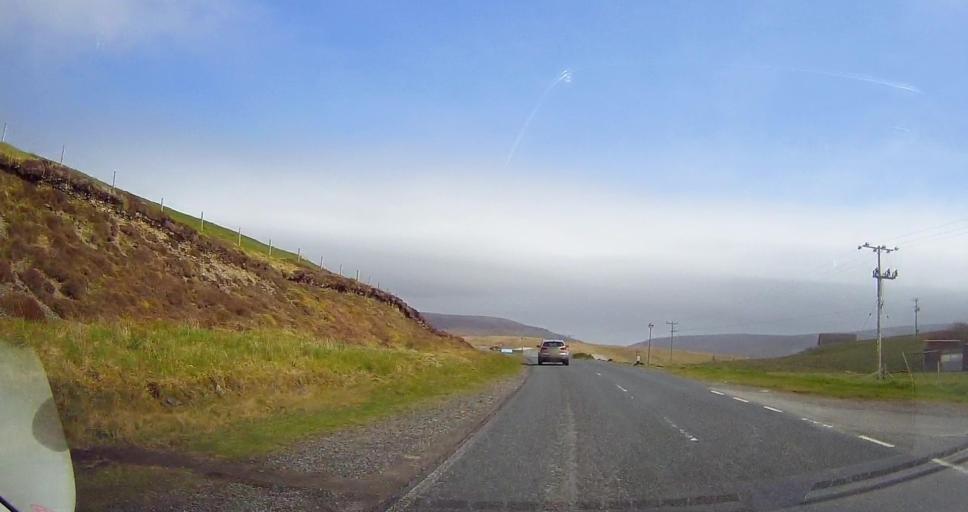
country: GB
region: Scotland
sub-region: Shetland Islands
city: Sandwick
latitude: 60.1048
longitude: -1.3195
